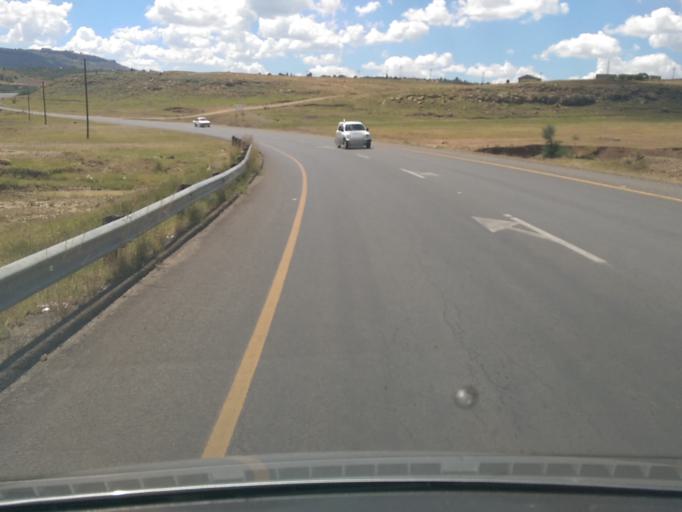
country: LS
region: Maseru
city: Maseru
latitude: -29.3886
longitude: 27.5049
